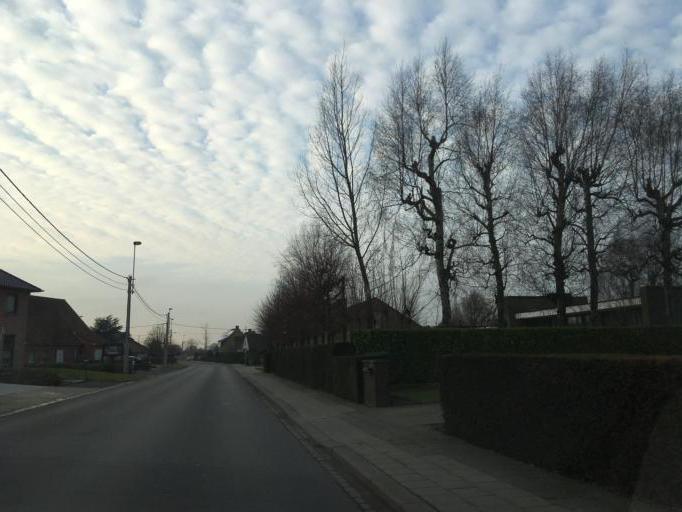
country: BE
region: Flanders
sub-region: Provincie West-Vlaanderen
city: Roeselare
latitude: 50.9290
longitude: 3.1122
